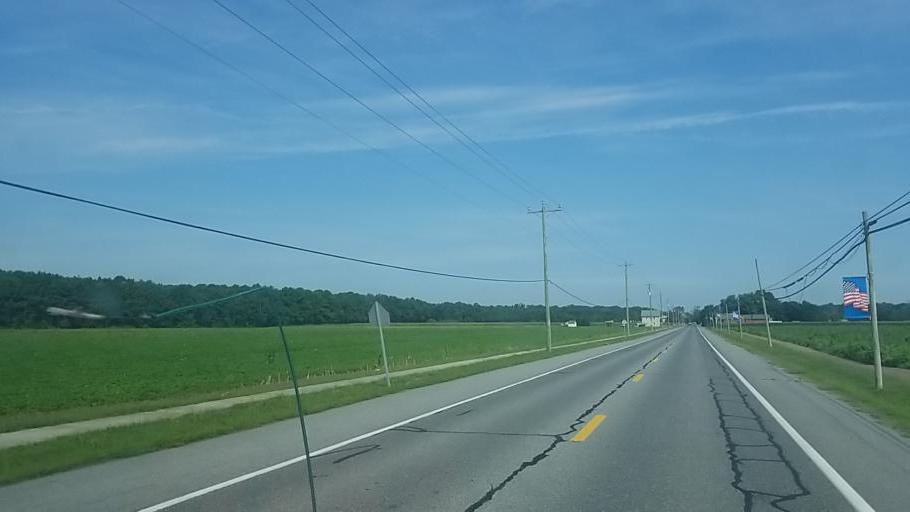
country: US
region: Delaware
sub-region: Sussex County
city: Millsboro
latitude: 38.5385
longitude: -75.2370
